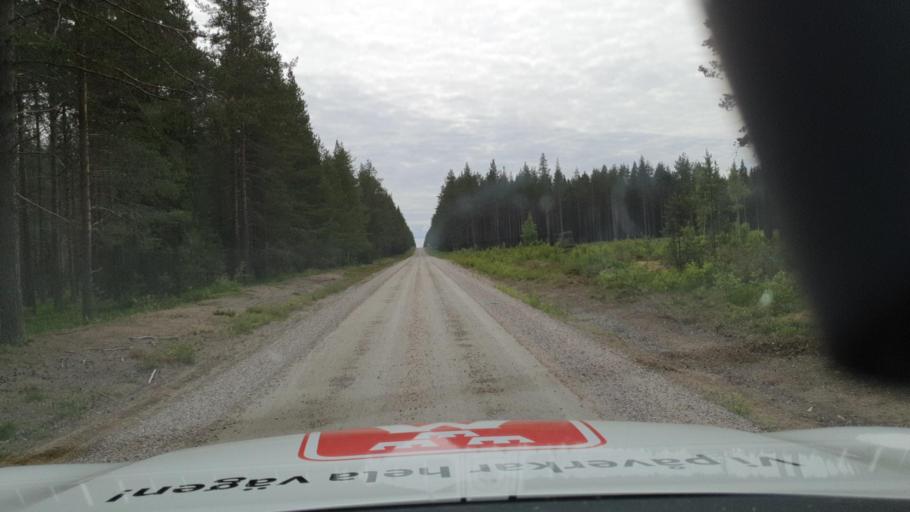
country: SE
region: Vaesterbotten
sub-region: Skelleftea Kommun
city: Forsbacka
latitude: 64.6534
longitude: 20.4420
